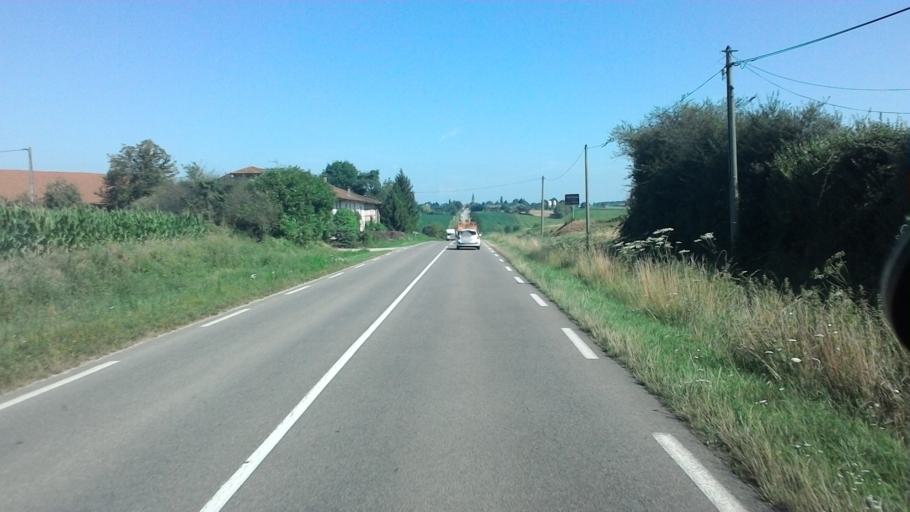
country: FR
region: Rhone-Alpes
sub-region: Departement de l'Ain
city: Saint-Trivier-de-Courtes
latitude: 46.4448
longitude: 5.0894
